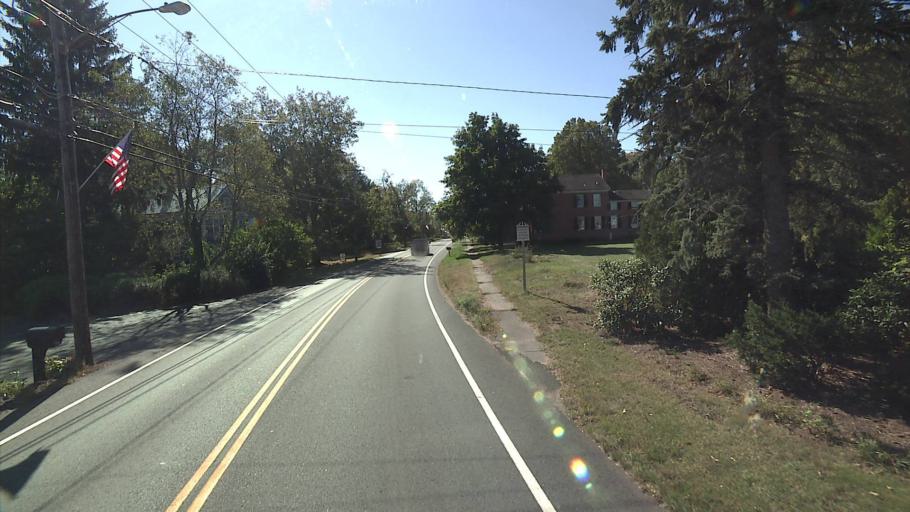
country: US
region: Connecticut
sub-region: Tolland County
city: Somers
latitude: 41.9896
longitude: -72.4478
